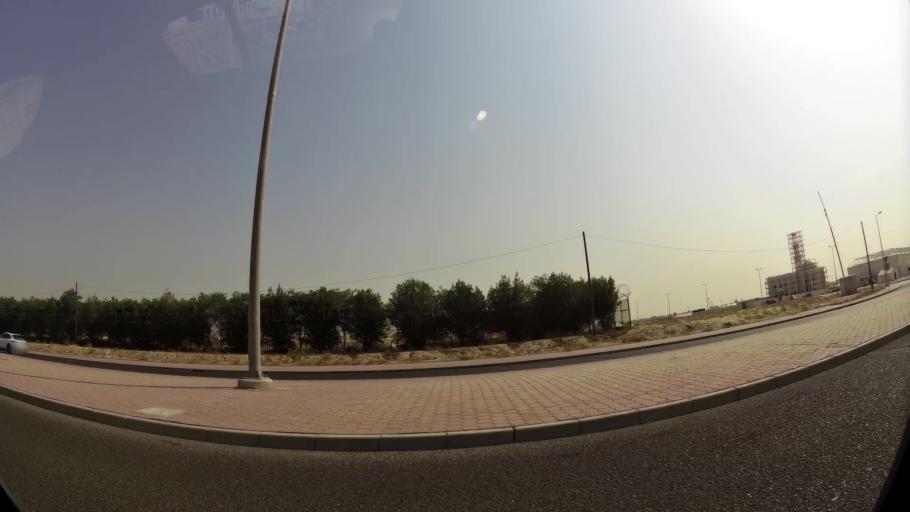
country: KW
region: Al Asimah
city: Ar Rabiyah
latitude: 29.2825
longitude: 47.9145
